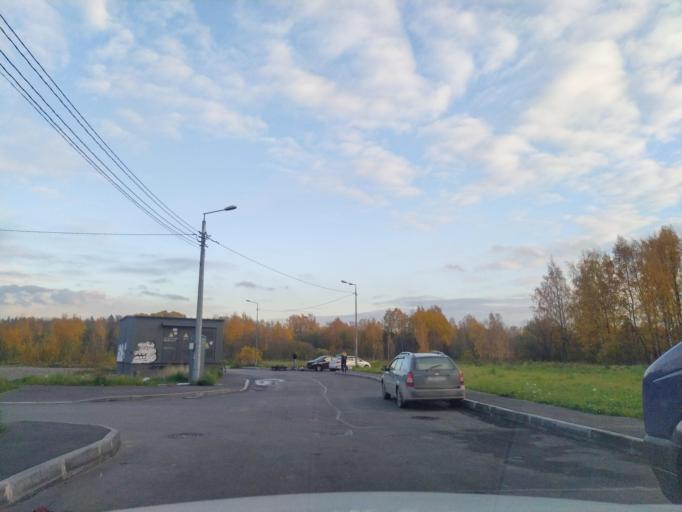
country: RU
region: Leningrad
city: Murino
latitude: 60.0318
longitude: 30.4617
